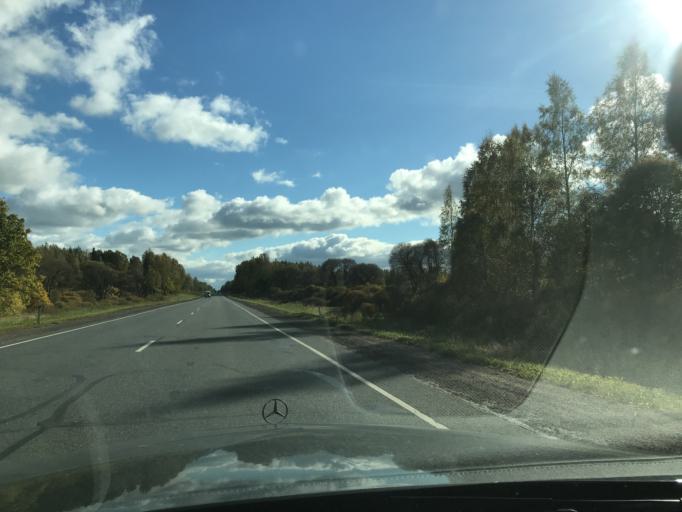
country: RU
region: Pskov
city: Ostrov
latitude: 57.2125
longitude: 28.4539
